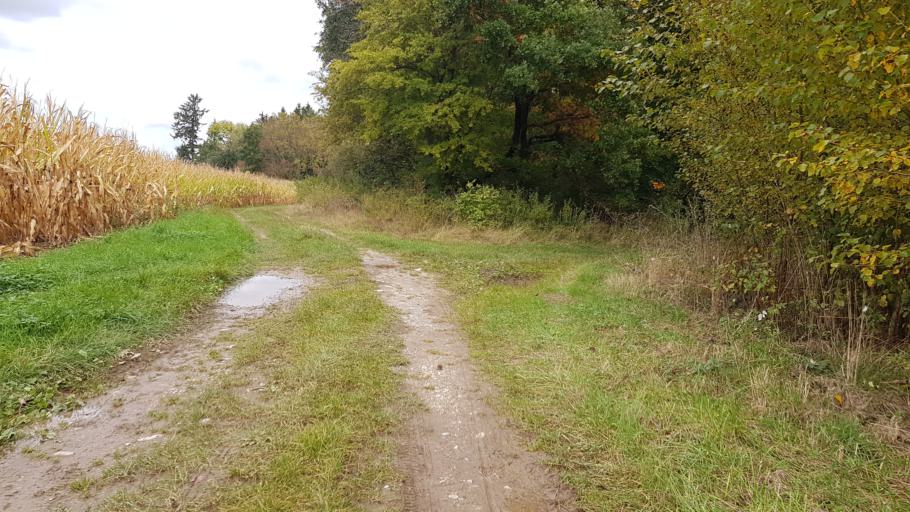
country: DE
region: Bavaria
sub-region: Upper Bavaria
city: Gilching
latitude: 48.1027
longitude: 11.3407
